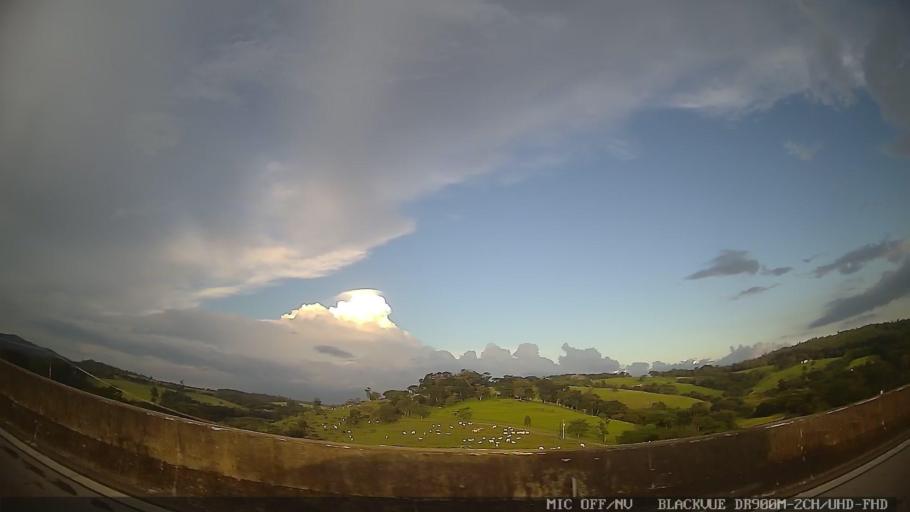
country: BR
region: Sao Paulo
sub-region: Itatiba
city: Itatiba
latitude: -23.0067
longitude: -46.7667
